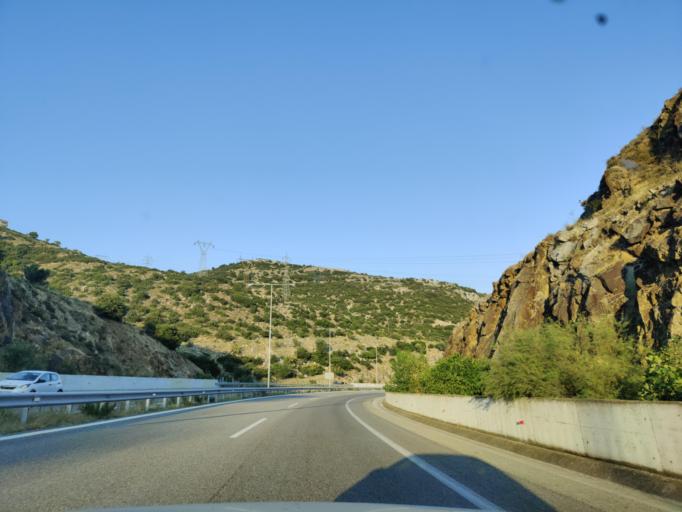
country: GR
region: East Macedonia and Thrace
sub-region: Nomos Kavalas
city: Kavala
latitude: 40.9602
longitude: 24.4404
